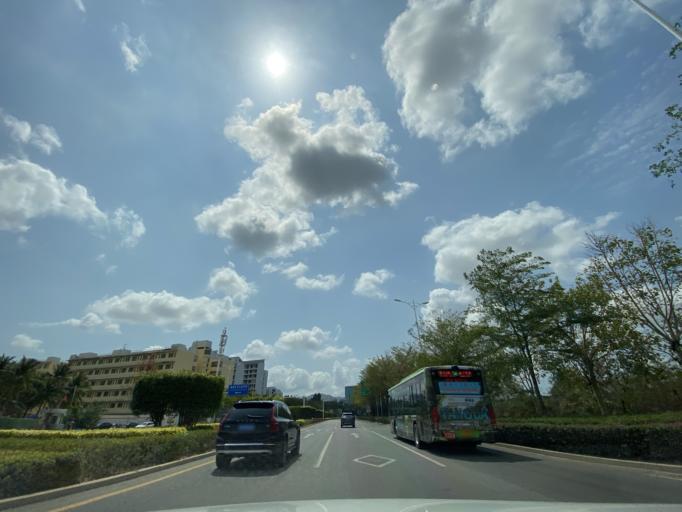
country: CN
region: Hainan
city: Tiandu
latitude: 18.3193
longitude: 109.5258
